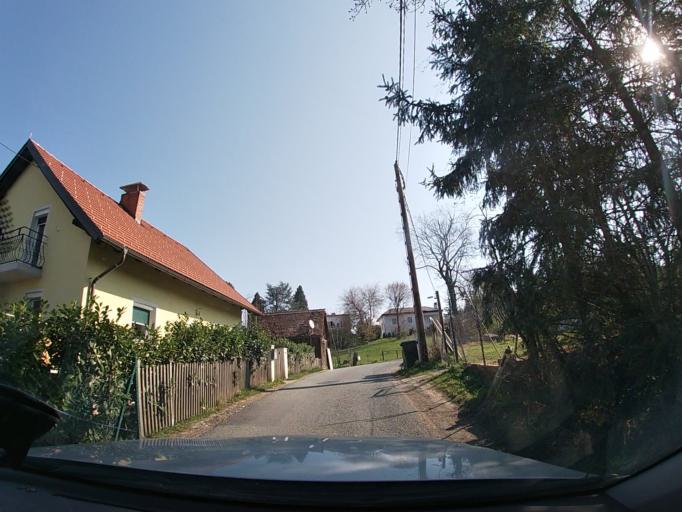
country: AT
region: Styria
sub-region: Politischer Bezirk Graz-Umgebung
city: Raaba
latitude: 47.0432
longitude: 15.4902
